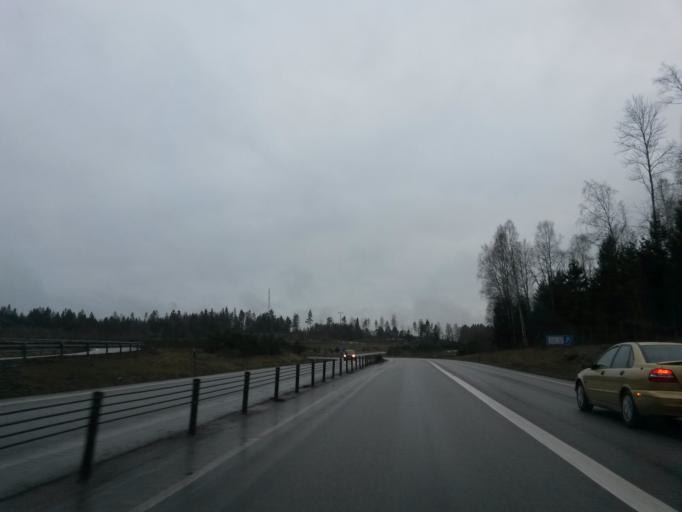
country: SE
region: Vaestra Goetaland
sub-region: Uddevalla Kommun
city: Uddevalla
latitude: 58.3386
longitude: 11.9871
